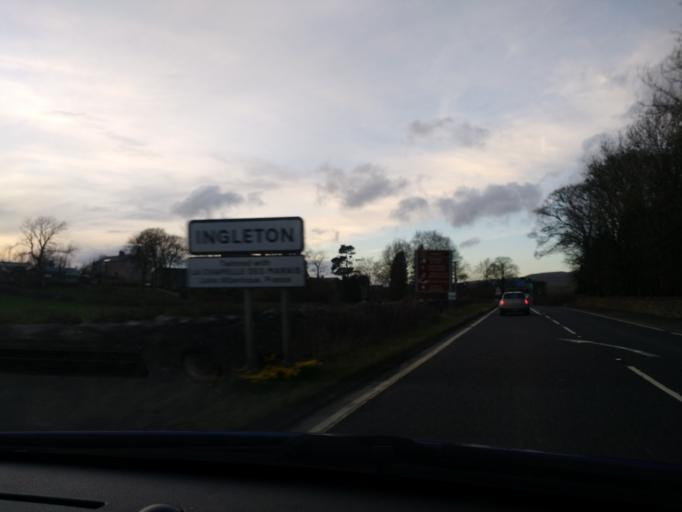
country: GB
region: England
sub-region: North Yorkshire
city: Ingleton
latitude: 54.1421
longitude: -2.4629
